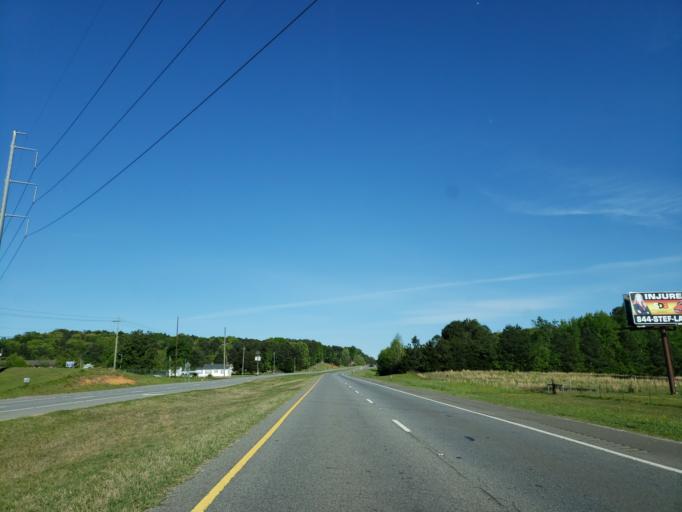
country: US
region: Georgia
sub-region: Polk County
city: Cedartown
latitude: 34.0136
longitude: -85.1894
